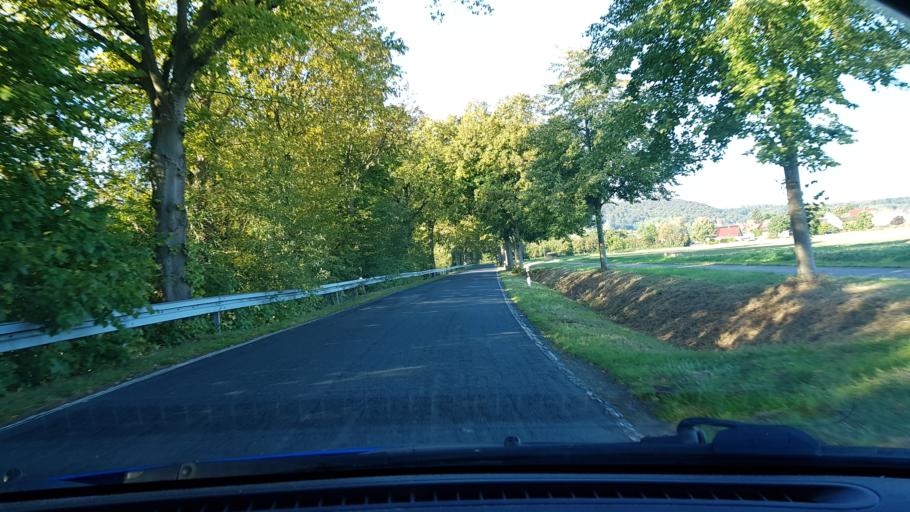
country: DE
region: Lower Saxony
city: Messenkamp
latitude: 52.2126
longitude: 9.3970
